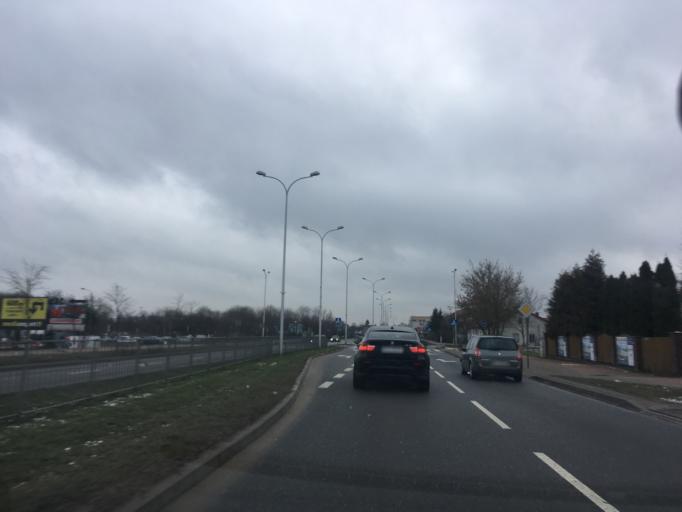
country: PL
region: Podlasie
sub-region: Suwalki
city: Suwalki
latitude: 54.1147
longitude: 22.9285
